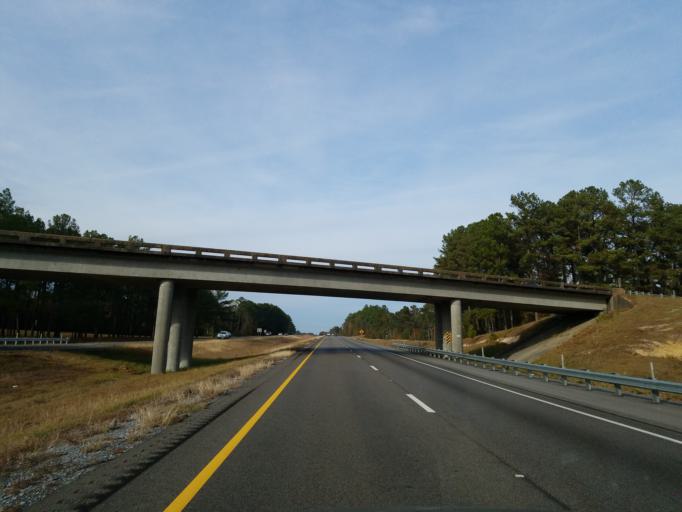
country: US
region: Mississippi
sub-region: Jones County
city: Sharon
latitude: 31.7844
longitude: -89.0553
